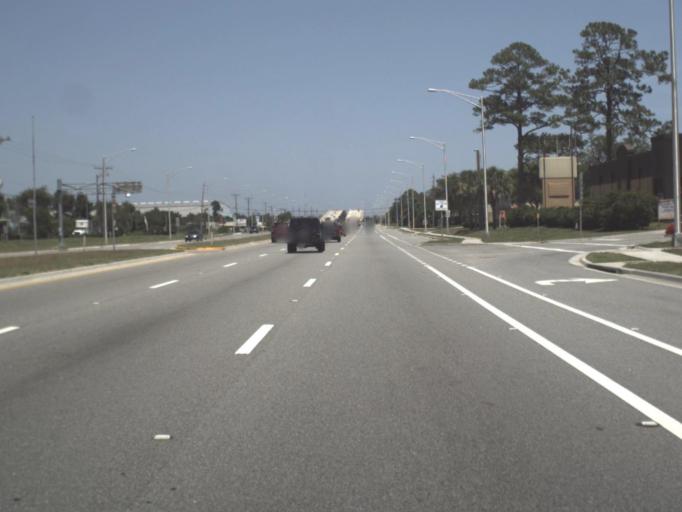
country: US
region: Florida
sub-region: Duval County
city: Jacksonville Beach
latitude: 30.2878
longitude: -81.4365
